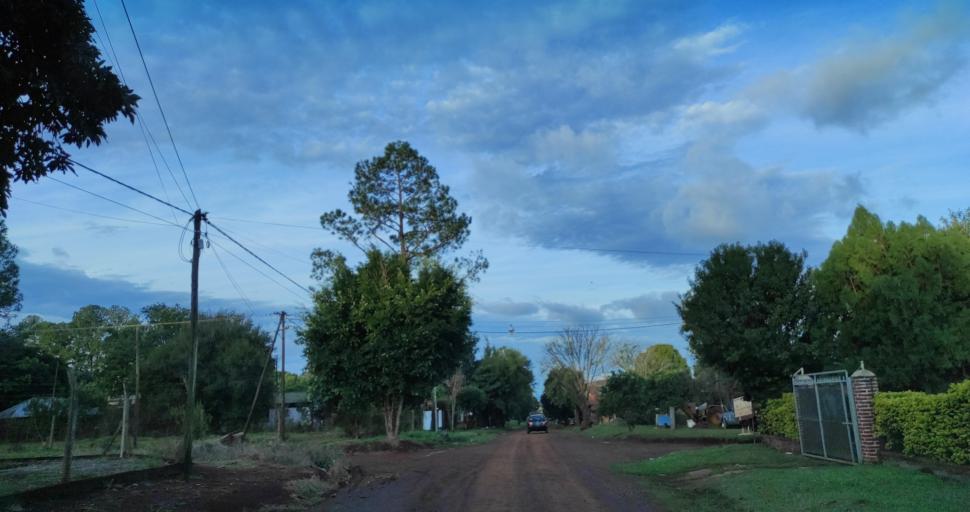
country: AR
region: Misiones
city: Garupa
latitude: -27.4818
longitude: -55.8613
